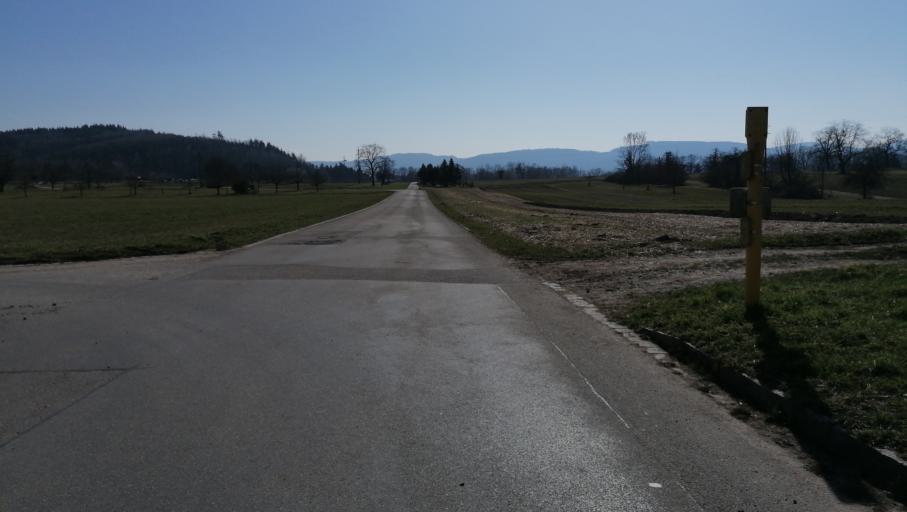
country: DE
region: Baden-Wuerttemberg
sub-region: Freiburg Region
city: Schworstadt
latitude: 47.5876
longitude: 7.9171
